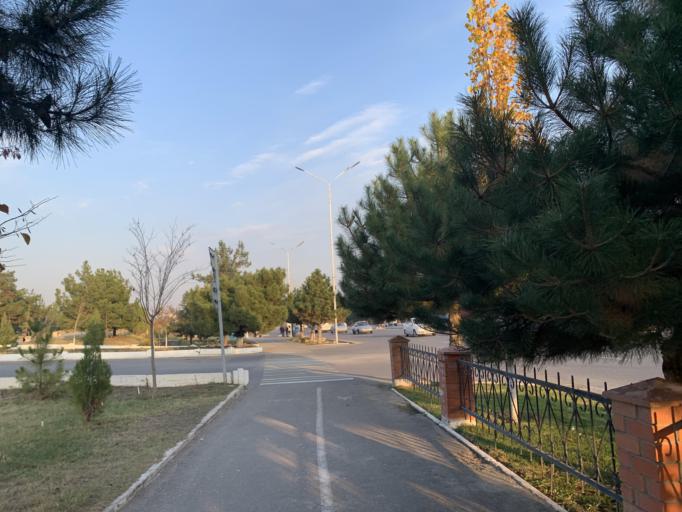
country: UZ
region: Namangan
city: Namangan Shahri
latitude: 41.0009
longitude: 71.6069
